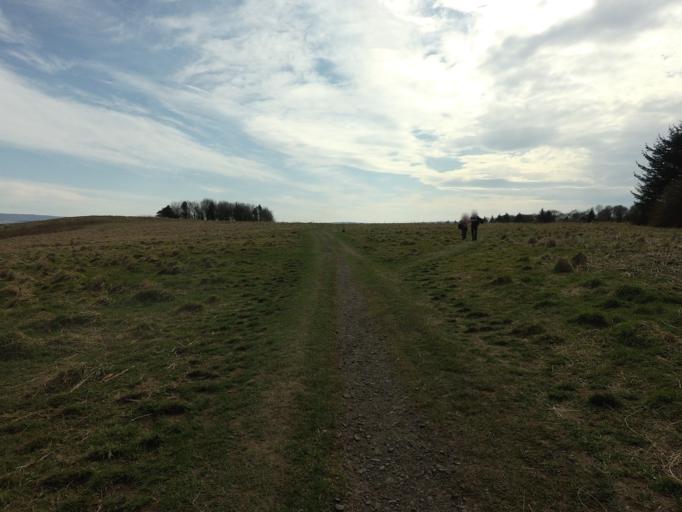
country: GB
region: Scotland
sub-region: West Lothian
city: Livingston
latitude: 55.9122
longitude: -3.5493
